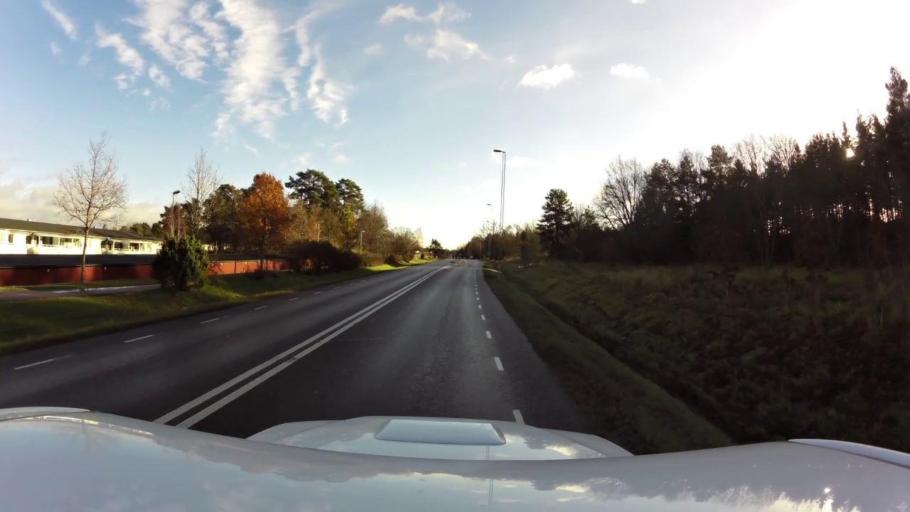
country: SE
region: OEstergoetland
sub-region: Linkopings Kommun
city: Linkoping
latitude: 58.3758
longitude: 15.6395
